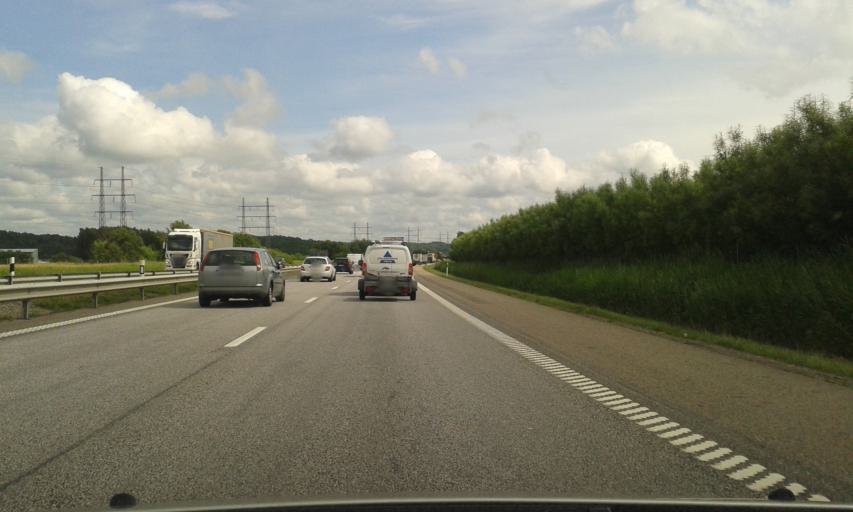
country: SE
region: Halland
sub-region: Kungsbacka Kommun
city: Kungsbacka
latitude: 57.4707
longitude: 12.0607
